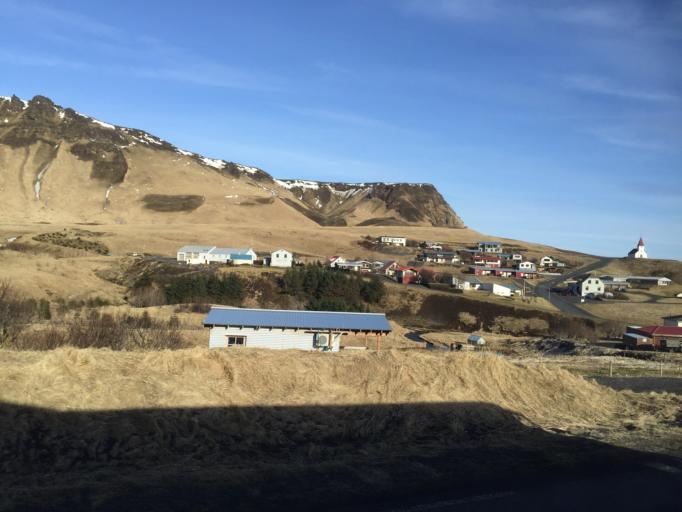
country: IS
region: South
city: Vestmannaeyjar
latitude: 63.4216
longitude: -19.0129
